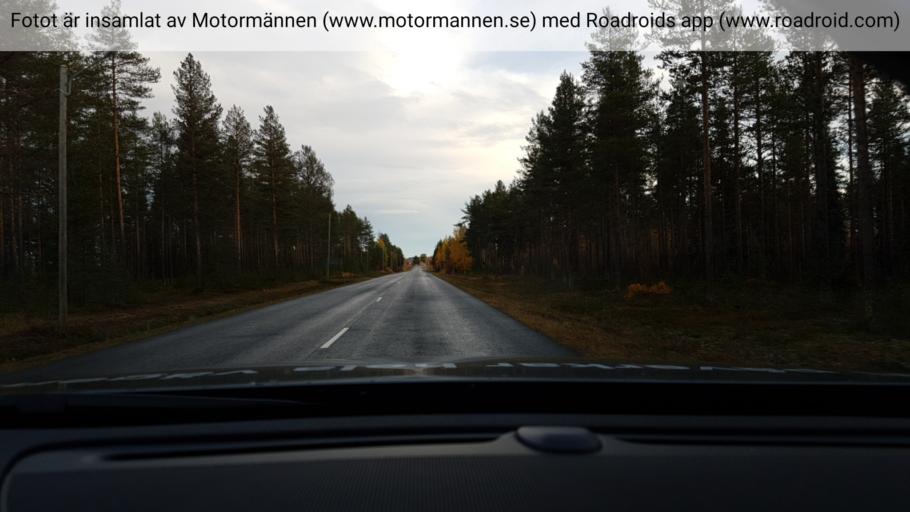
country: SE
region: Norrbotten
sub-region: Overkalix Kommun
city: OEverkalix
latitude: 66.9436
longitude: 22.7224
